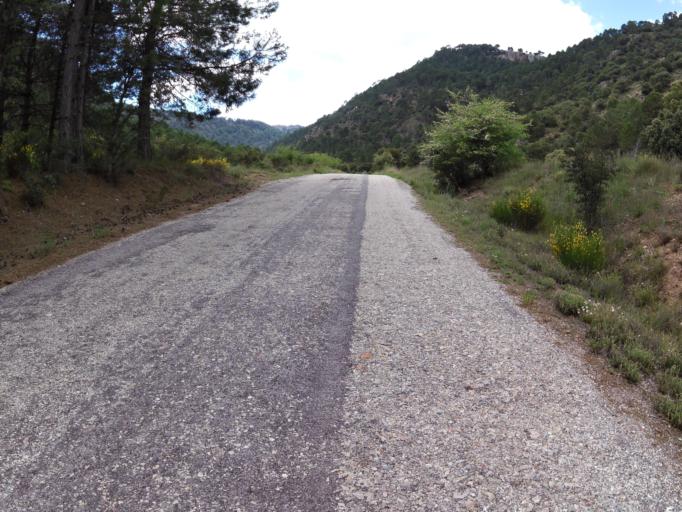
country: ES
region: Castille-La Mancha
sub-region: Provincia de Albacete
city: Paterna del Madera
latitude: 38.5793
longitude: -2.3488
